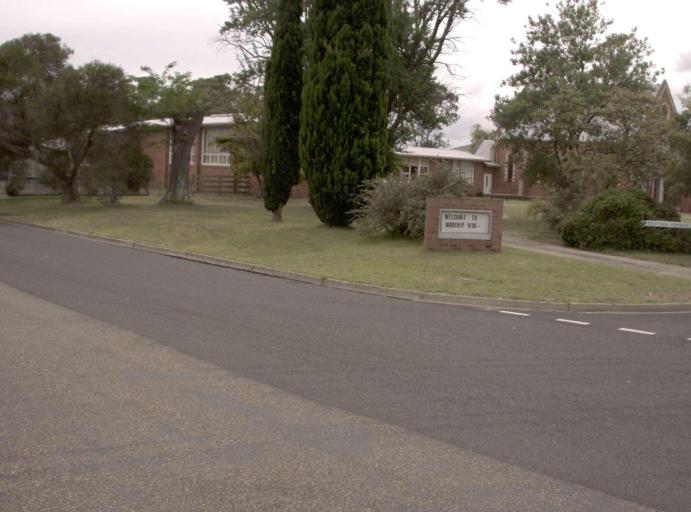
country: AU
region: Victoria
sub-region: Wellington
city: Sale
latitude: -37.9626
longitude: 147.0807
